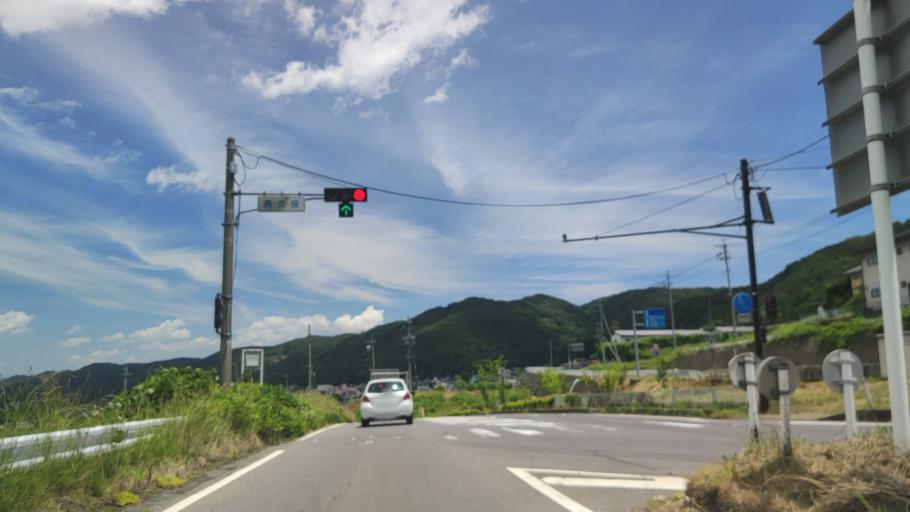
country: JP
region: Nagano
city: Kamimaruko
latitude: 36.2473
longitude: 138.2617
